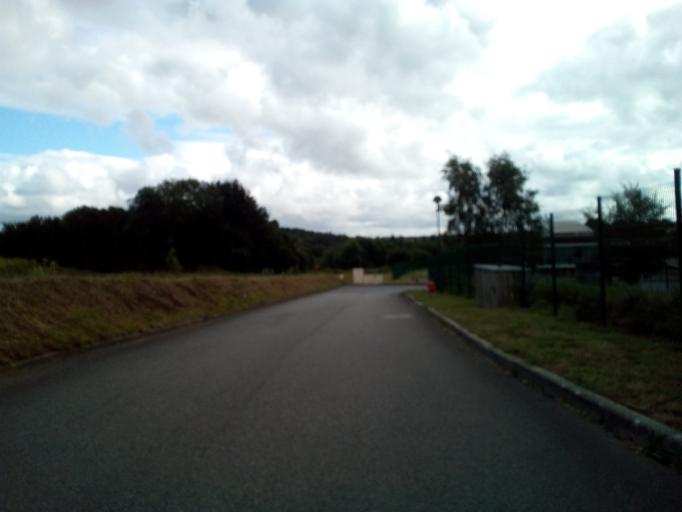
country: FR
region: Brittany
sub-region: Departement du Finistere
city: Landivisiau
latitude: 48.5117
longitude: -4.0532
